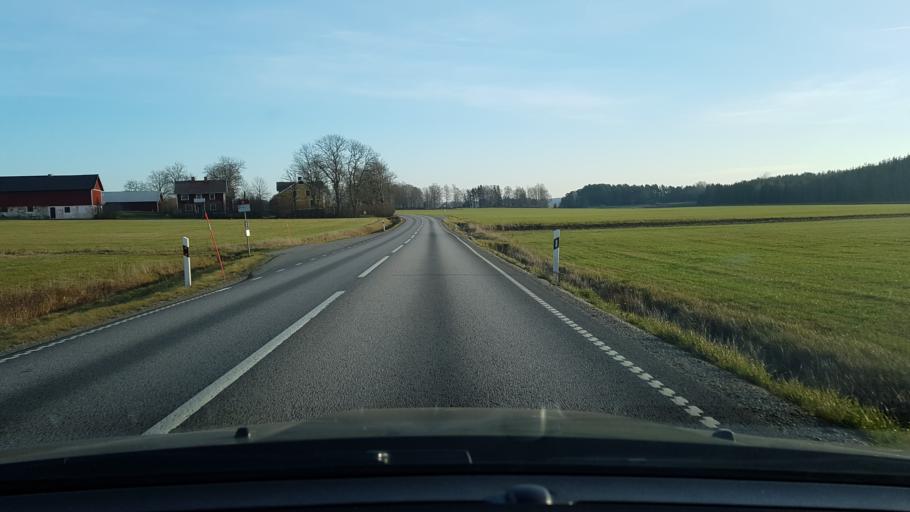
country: SE
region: Stockholm
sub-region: Norrtalje Kommun
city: Nykvarn
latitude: 59.7430
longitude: 18.1301
